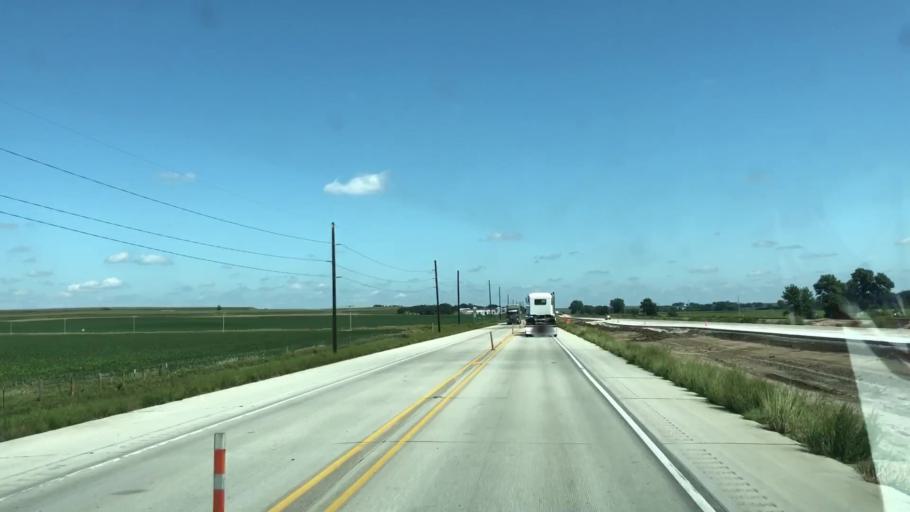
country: US
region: Iowa
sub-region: Plymouth County
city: Le Mars
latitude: 42.7281
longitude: -96.2352
